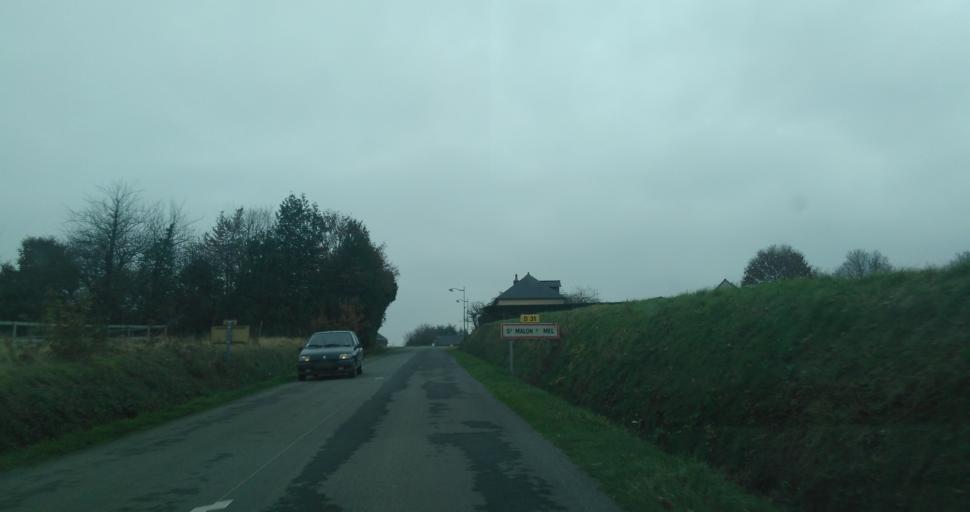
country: FR
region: Brittany
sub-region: Departement d'Ille-et-Vilaine
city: Iffendic
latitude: 48.0942
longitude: -2.1039
